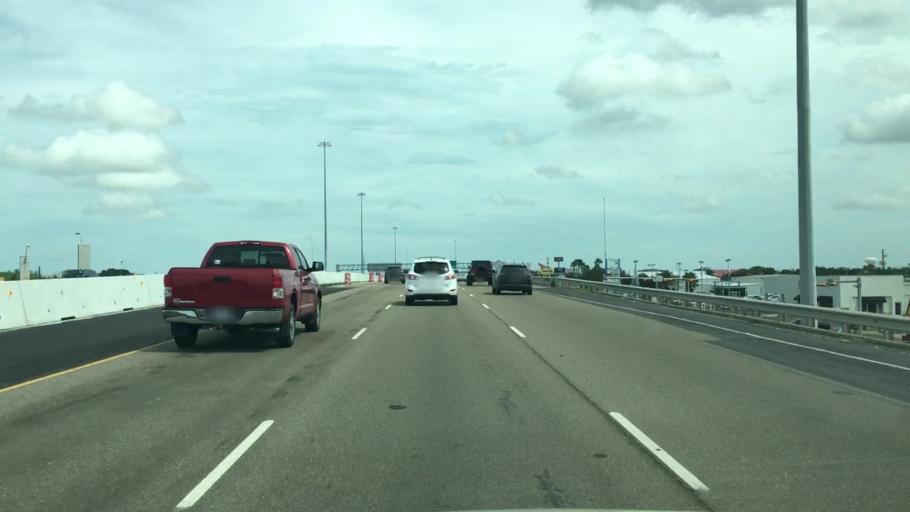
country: US
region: Texas
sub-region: Nueces County
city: Corpus Christi
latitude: 27.7255
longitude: -97.4067
